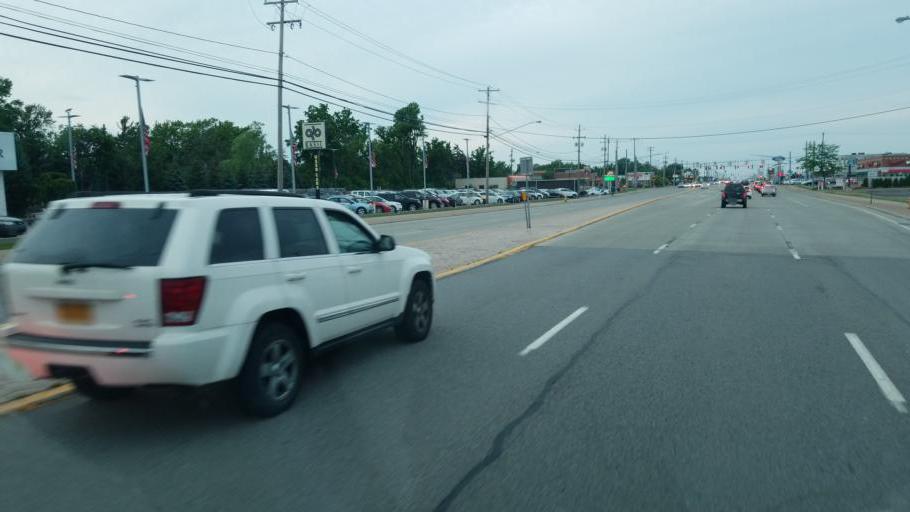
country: US
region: New York
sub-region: Erie County
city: Harris Hill
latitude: 42.9543
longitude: -78.6969
